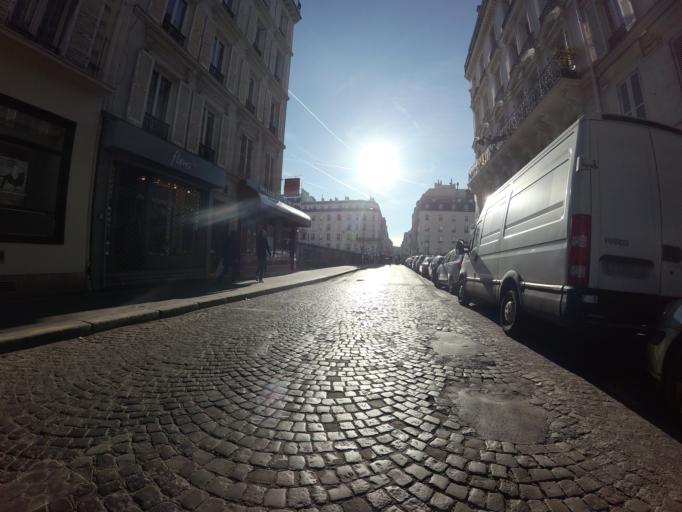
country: FR
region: Ile-de-France
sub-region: Departement des Hauts-de-Seine
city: Clichy
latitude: 48.8861
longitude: 2.3176
